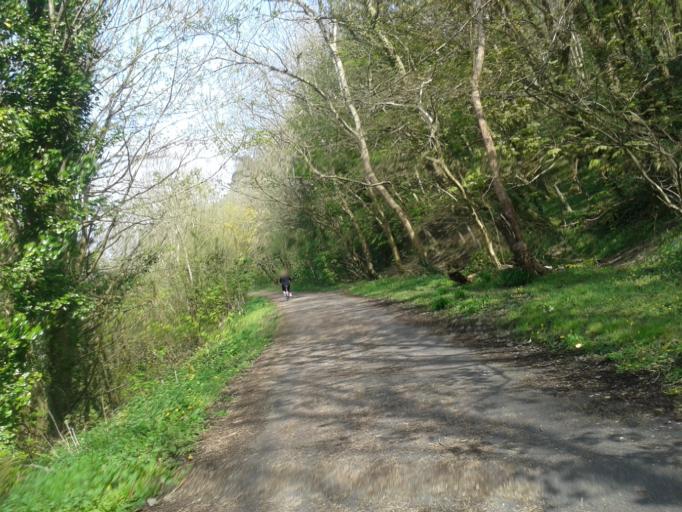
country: GB
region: England
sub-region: Devon
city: Ilfracombe
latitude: 51.1932
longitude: -4.1287
